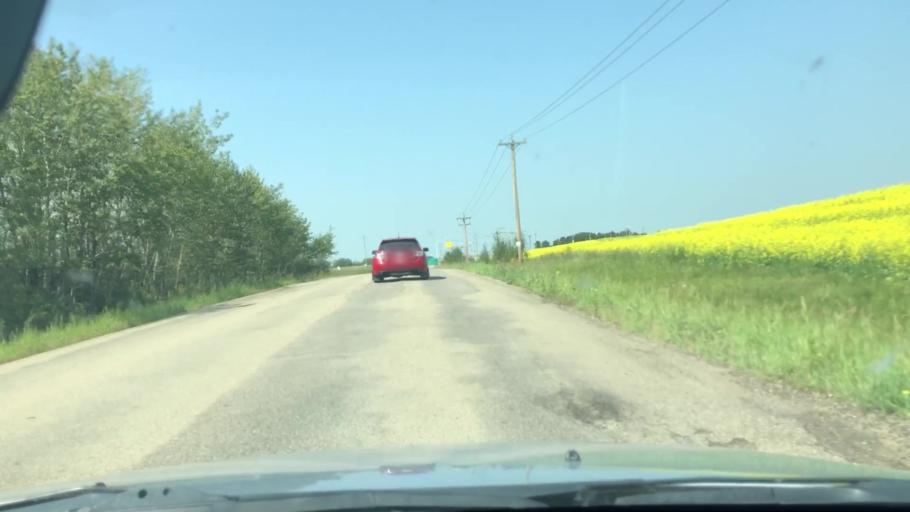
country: CA
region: Alberta
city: Devon
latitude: 53.5122
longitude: -113.7541
